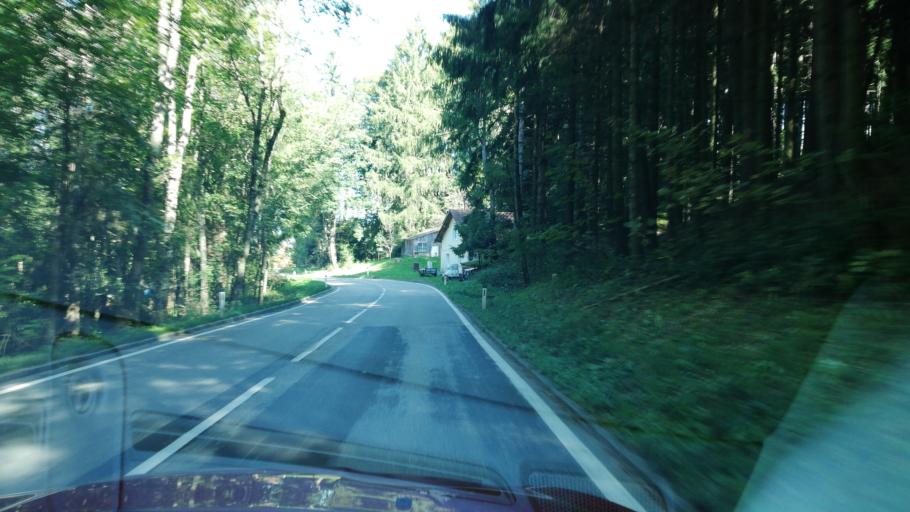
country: AT
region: Upper Austria
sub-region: Politischer Bezirk Vocklabruck
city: Zell am Pettenfirst
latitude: 48.1204
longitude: 13.5667
